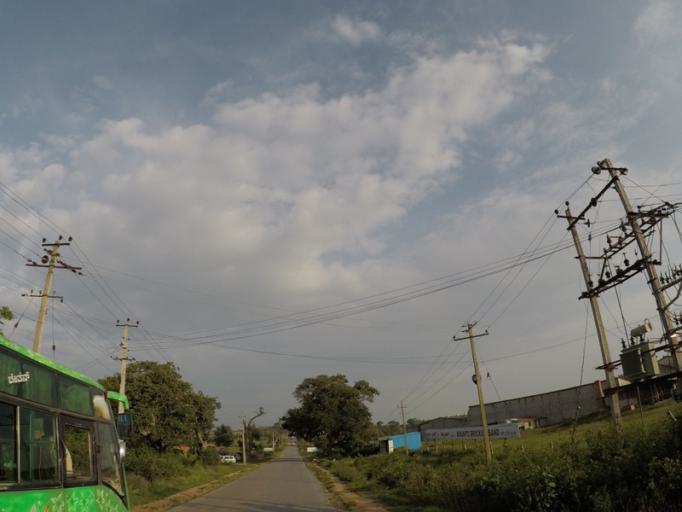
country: IN
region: Karnataka
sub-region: Chikmagalur
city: Chikmagalur
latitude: 13.2751
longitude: 75.8260
